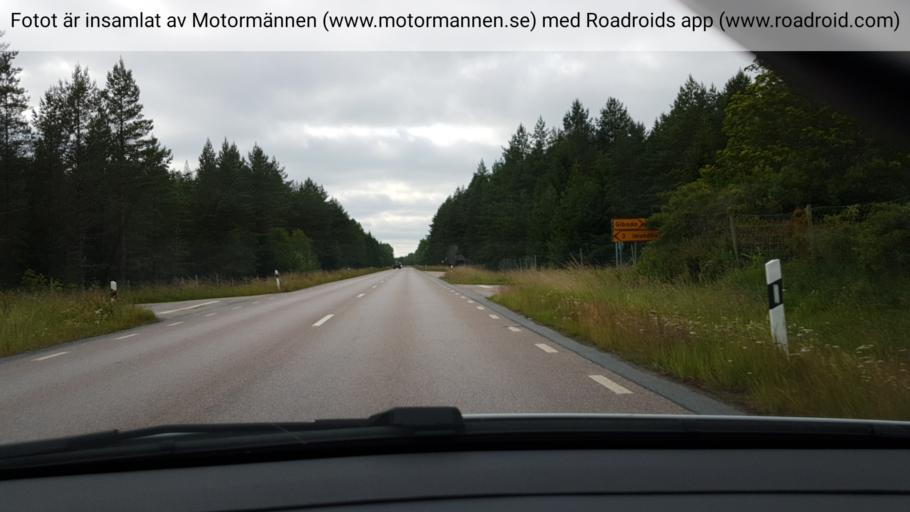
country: SE
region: Uppsala
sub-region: Osthammars Kommun
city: Osterbybruk
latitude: 60.3892
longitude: 17.9449
